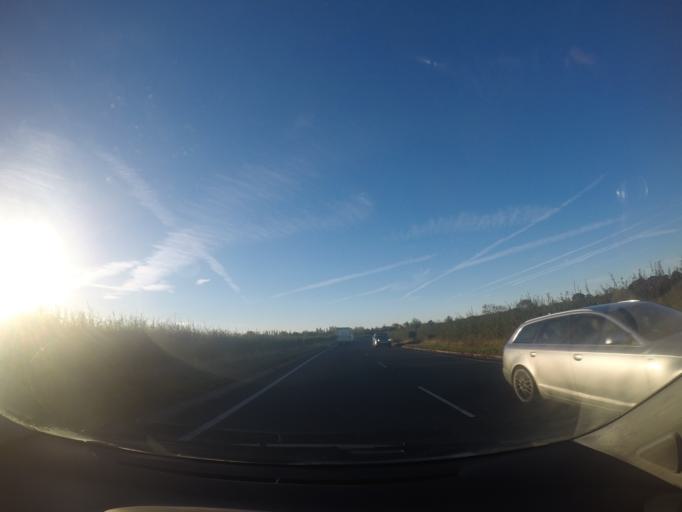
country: GB
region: England
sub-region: City of York
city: Copmanthorpe
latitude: 53.9295
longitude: -1.1441
